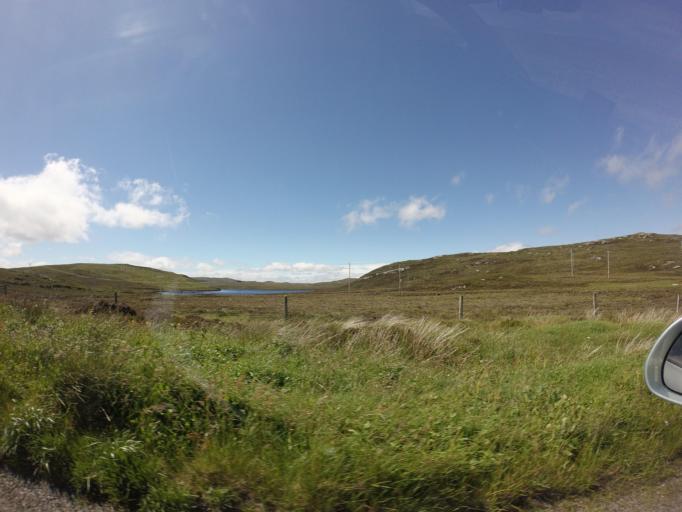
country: GB
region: Scotland
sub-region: Eilean Siar
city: Stornoway
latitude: 58.1260
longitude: -6.5073
